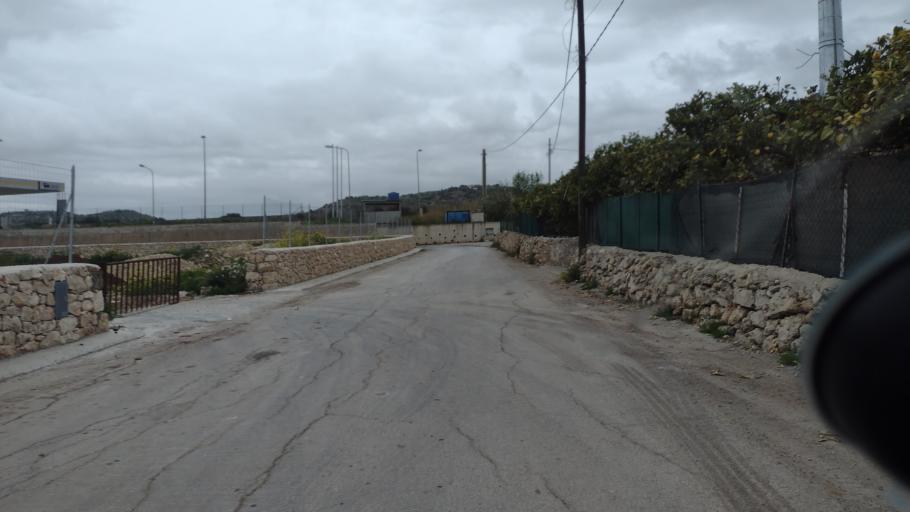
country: IT
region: Sicily
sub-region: Provincia di Siracusa
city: Avola
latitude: 36.8976
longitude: 15.1156
